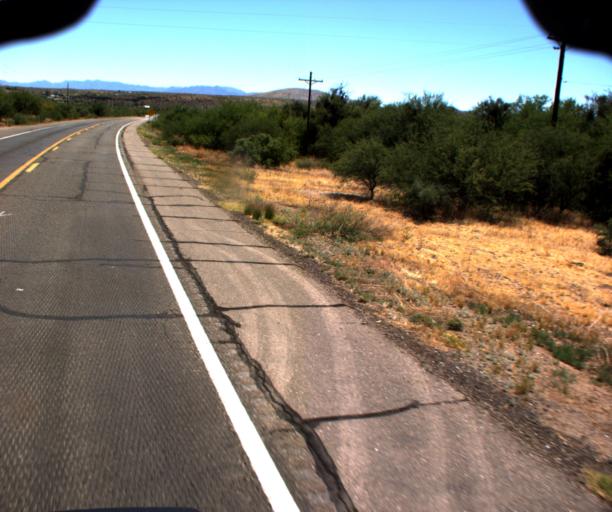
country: US
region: Arizona
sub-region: Pinal County
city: Mammoth
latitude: 32.7475
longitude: -110.6464
